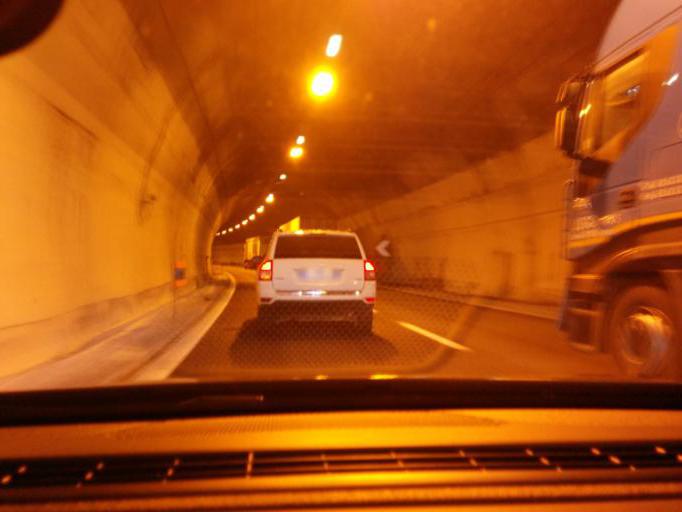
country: IT
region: Liguria
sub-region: Provincia di Savona
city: Varazze
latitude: 44.3665
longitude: 8.5701
